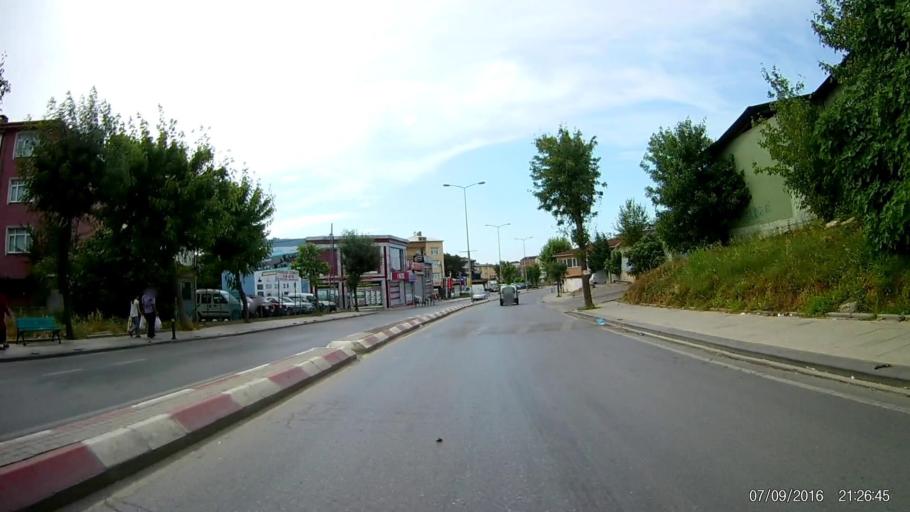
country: TR
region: Istanbul
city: Sultanbeyli
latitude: 40.9829
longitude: 29.2659
